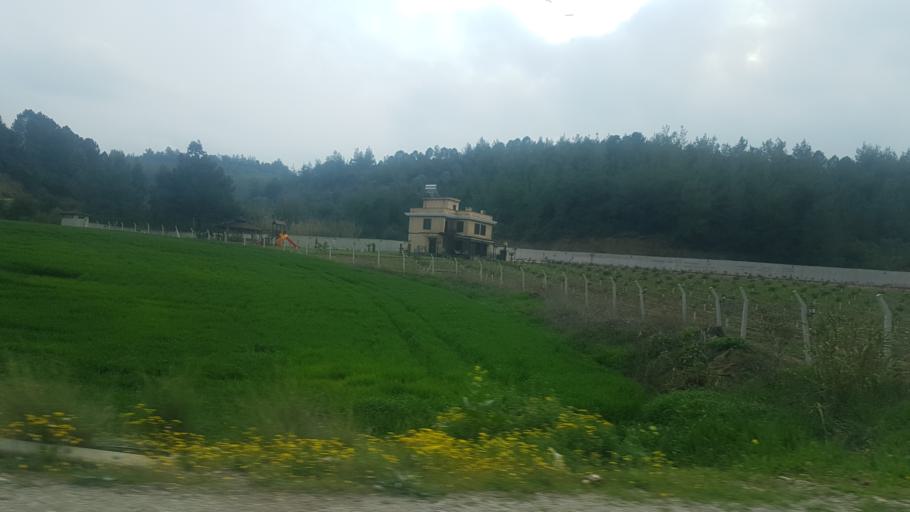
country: TR
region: Mersin
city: Yenice
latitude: 37.0901
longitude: 35.1525
